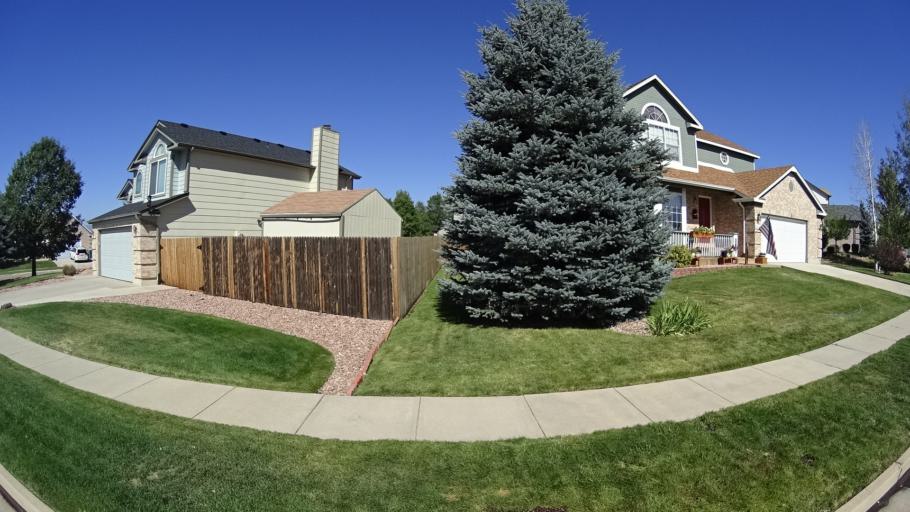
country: US
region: Colorado
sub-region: El Paso County
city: Black Forest
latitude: 38.9471
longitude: -104.7249
